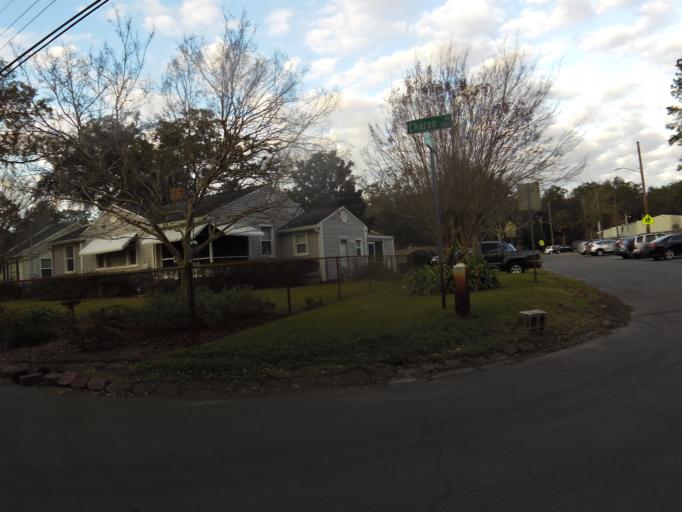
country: US
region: Florida
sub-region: Duval County
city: Jacksonville
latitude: 30.2919
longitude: -81.7152
